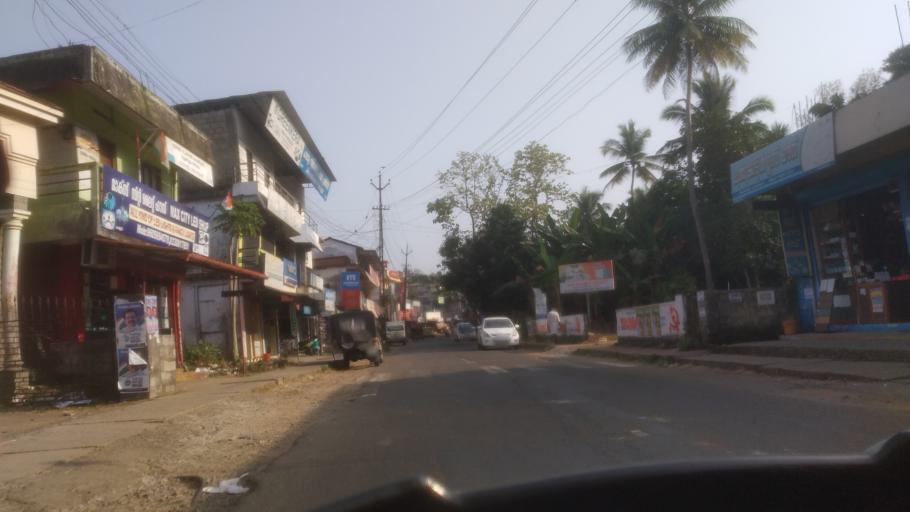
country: IN
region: Kerala
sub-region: Ernakulam
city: Piravam
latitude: 9.8286
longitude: 76.5015
